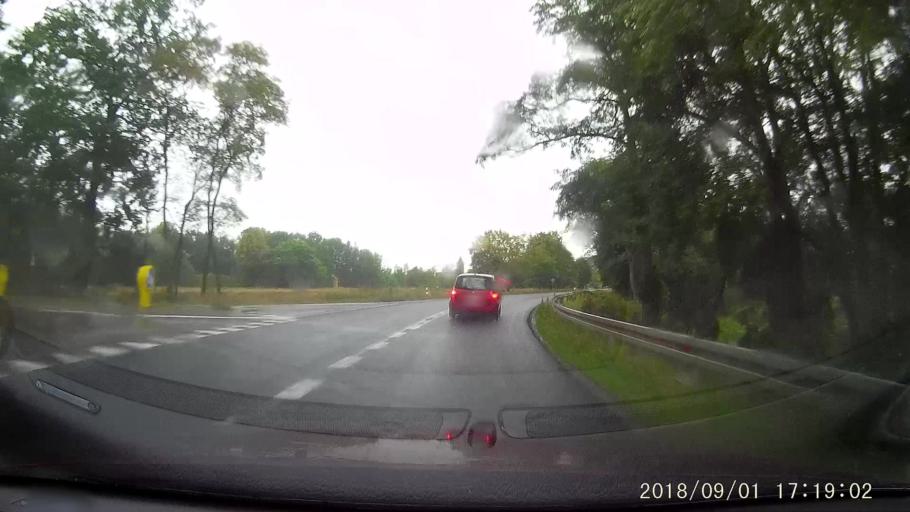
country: PL
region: Lubusz
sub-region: Powiat zielonogorski
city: Nowogrod Bobrzanski
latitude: 51.7340
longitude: 15.2747
